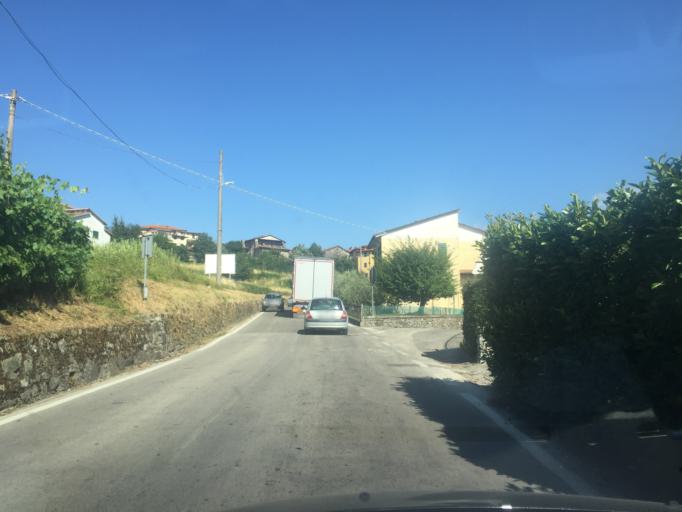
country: IT
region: Tuscany
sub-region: Provincia di Lucca
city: San Romano in Garfagnana
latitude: 44.1463
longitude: 10.3555
